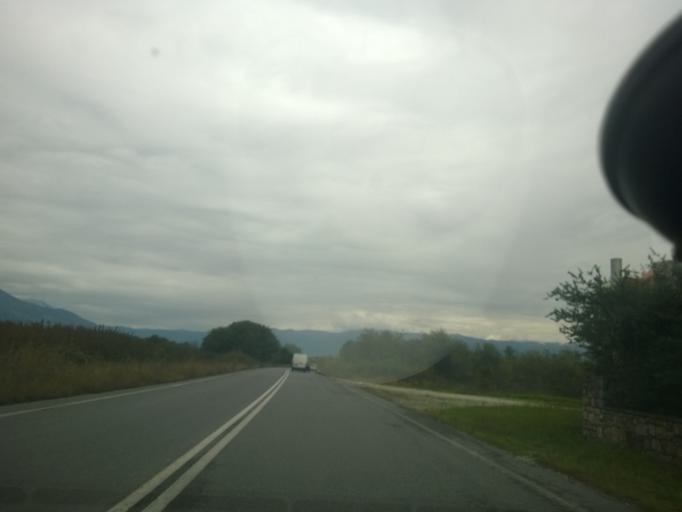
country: GR
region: Central Macedonia
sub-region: Nomos Pellis
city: Loutraki
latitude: 40.9710
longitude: 21.9834
